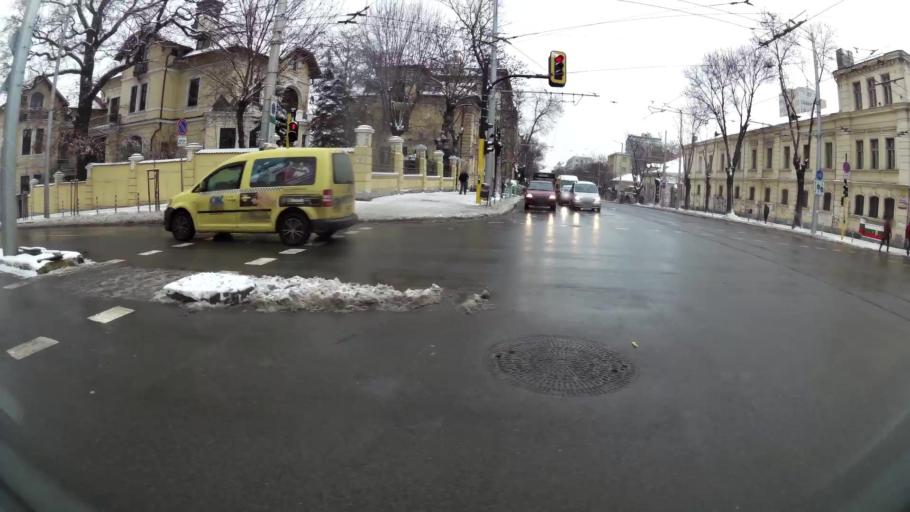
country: BG
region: Sofia-Capital
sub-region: Stolichna Obshtina
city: Sofia
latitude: 42.6988
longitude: 23.3347
